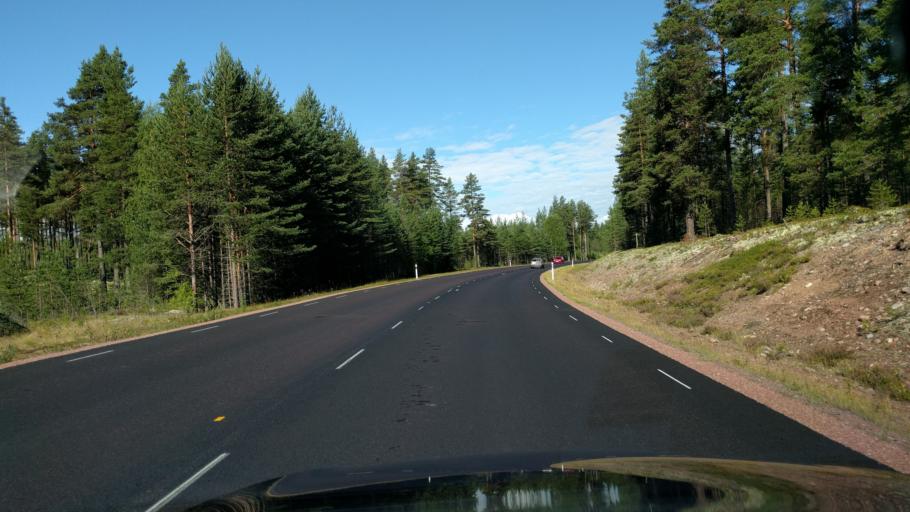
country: SE
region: Dalarna
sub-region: Alvdalens Kommun
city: AElvdalen
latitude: 61.1245
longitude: 14.1971
